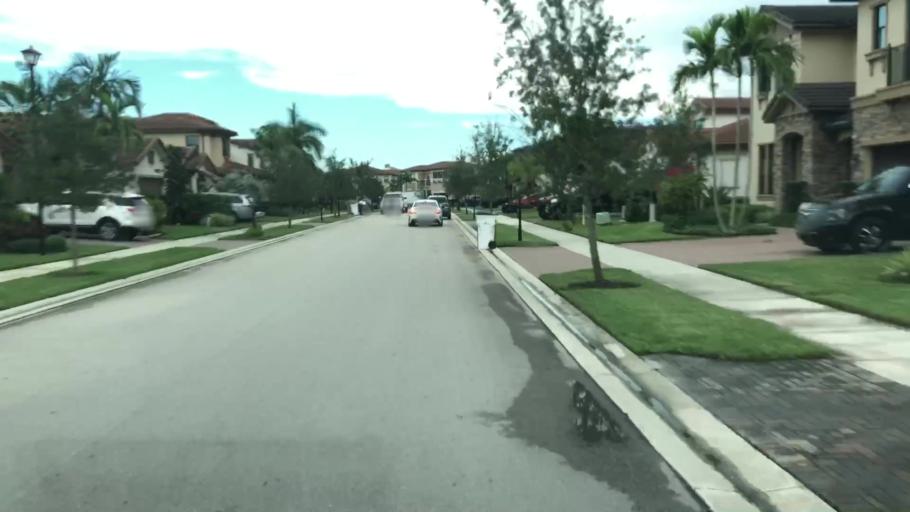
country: US
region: Florida
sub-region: Broward County
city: Parkland
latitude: 26.3429
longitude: -80.2759
